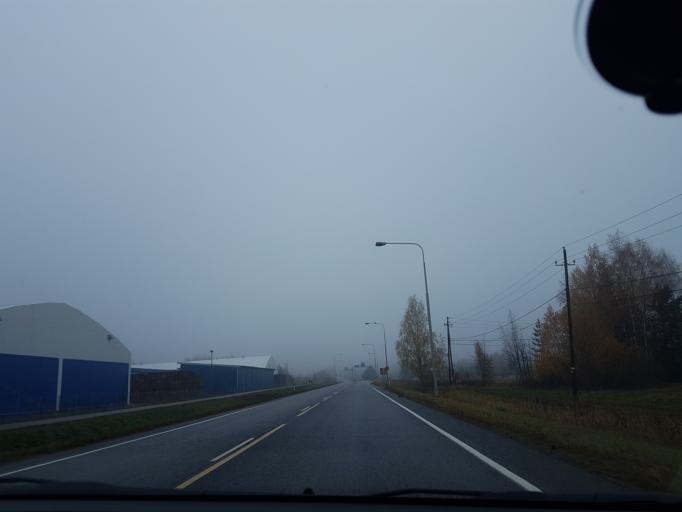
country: FI
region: Uusimaa
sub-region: Helsinki
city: Jaervenpaeae
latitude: 60.4670
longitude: 25.1407
